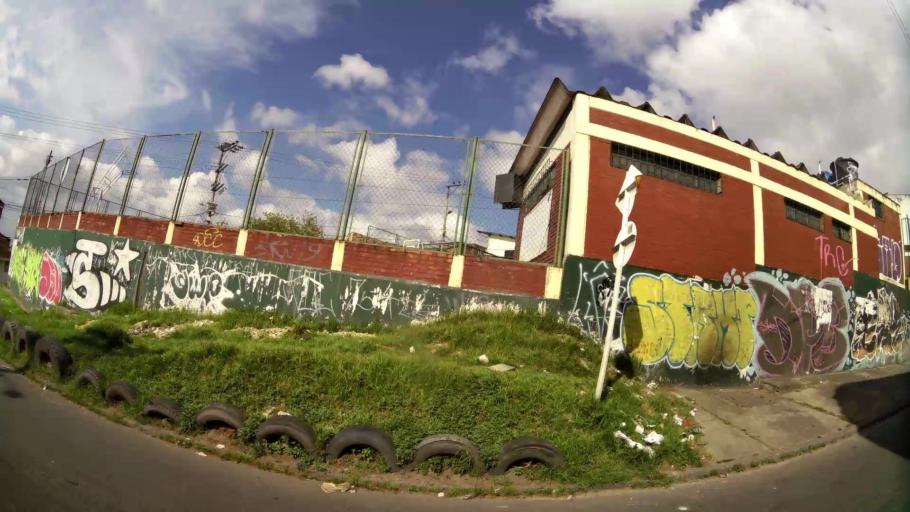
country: CO
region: Bogota D.C.
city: Bogota
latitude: 4.5442
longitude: -74.0894
